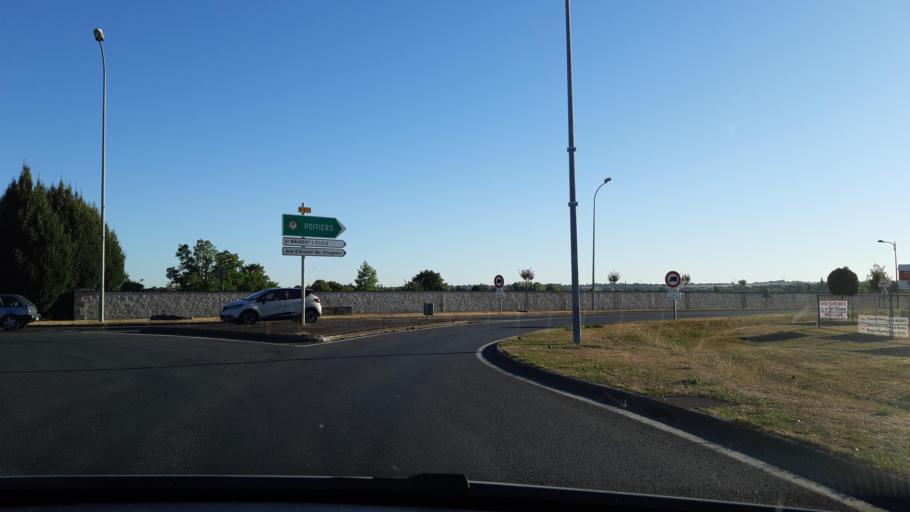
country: FR
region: Poitou-Charentes
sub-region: Departement des Deux-Sevres
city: La Creche
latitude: 46.3555
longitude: -0.3115
